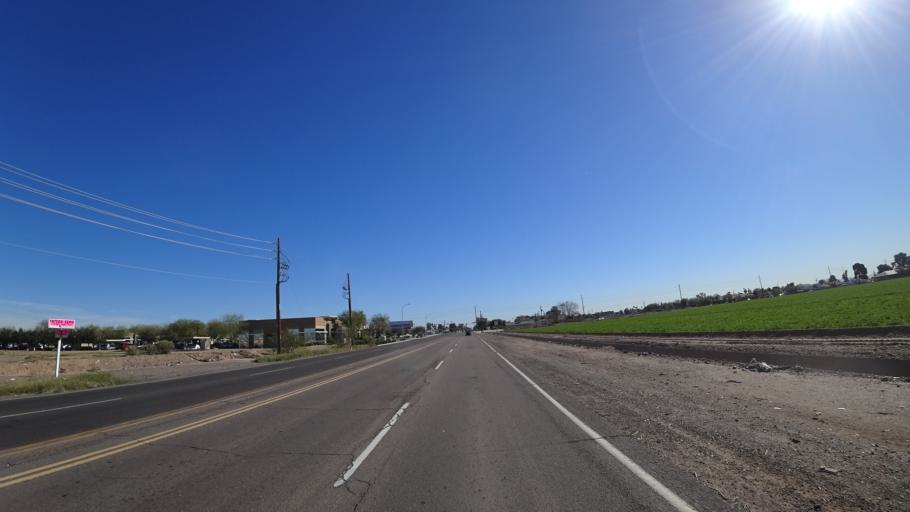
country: US
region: Arizona
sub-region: Maricopa County
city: Tolleson
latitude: 33.4941
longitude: -112.2582
